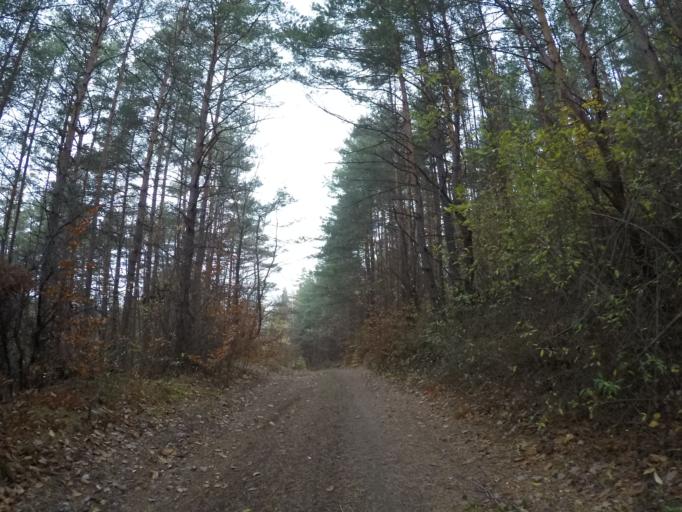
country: SK
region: Presovsky
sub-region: Okres Presov
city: Presov
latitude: 48.8978
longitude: 21.1642
